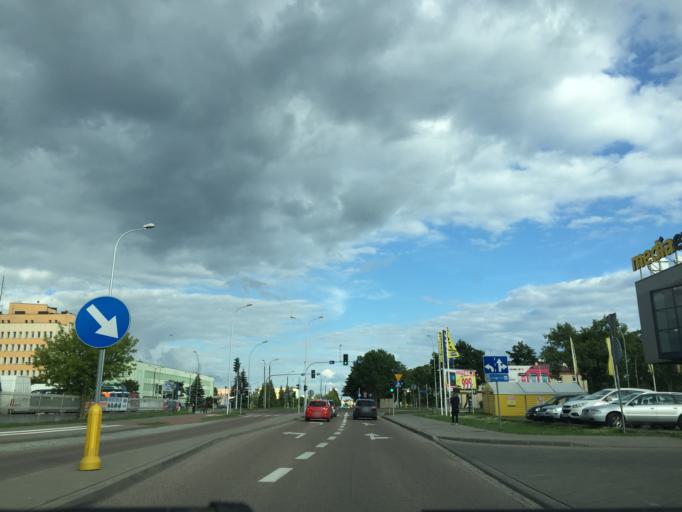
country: PL
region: Podlasie
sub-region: Suwalki
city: Suwalki
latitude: 54.1166
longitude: 22.9341
